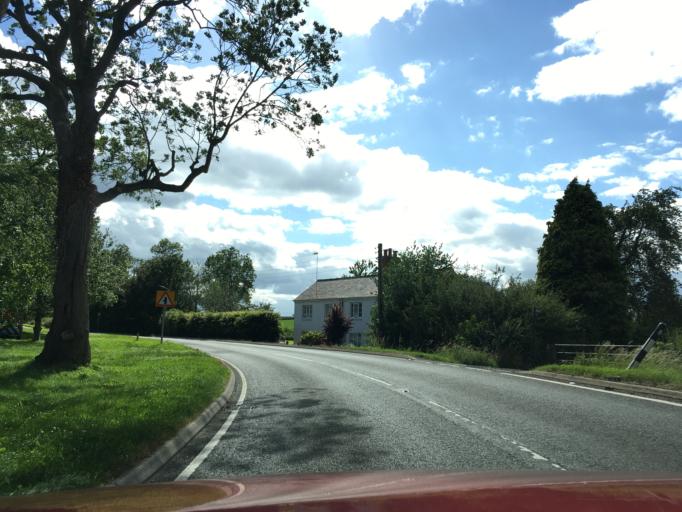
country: GB
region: England
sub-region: Leicestershire
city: Coalville
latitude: 52.7736
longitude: -1.3722
